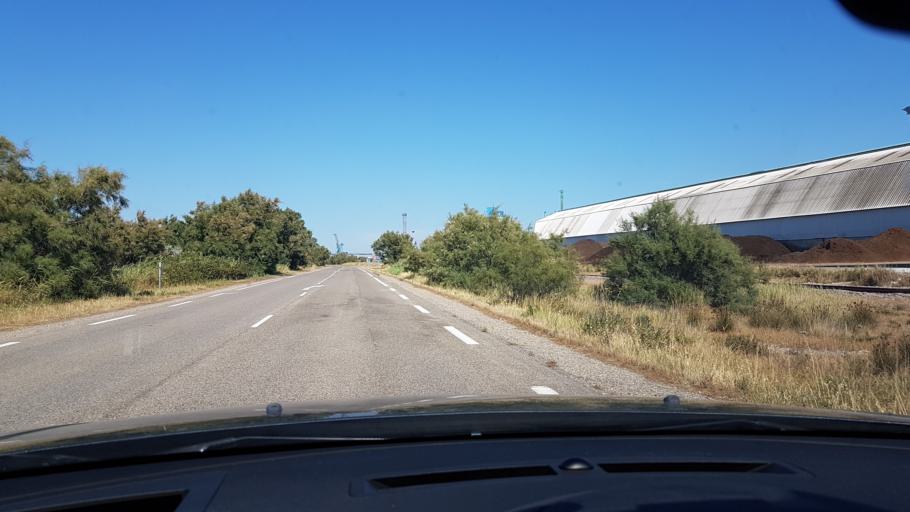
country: FR
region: Provence-Alpes-Cote d'Azur
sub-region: Departement des Bouches-du-Rhone
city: Port-Saint-Louis-du-Rhone
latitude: 43.3914
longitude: 4.8325
